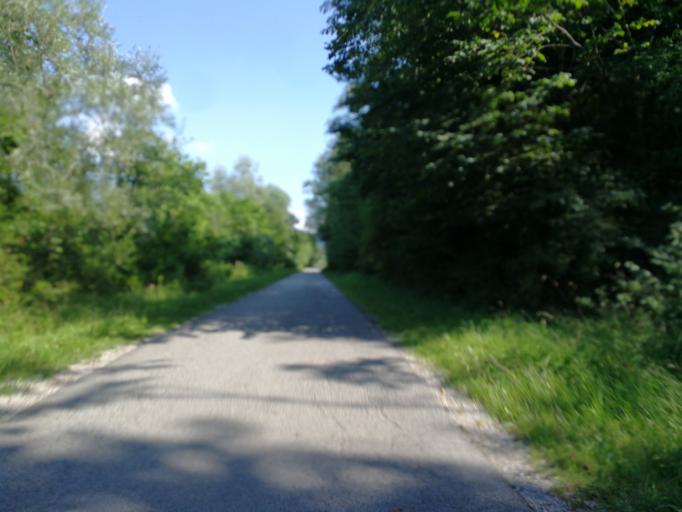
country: AT
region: Salzburg
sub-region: Politischer Bezirk Salzburg-Umgebung
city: Bergheim
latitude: 47.8349
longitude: 13.0234
